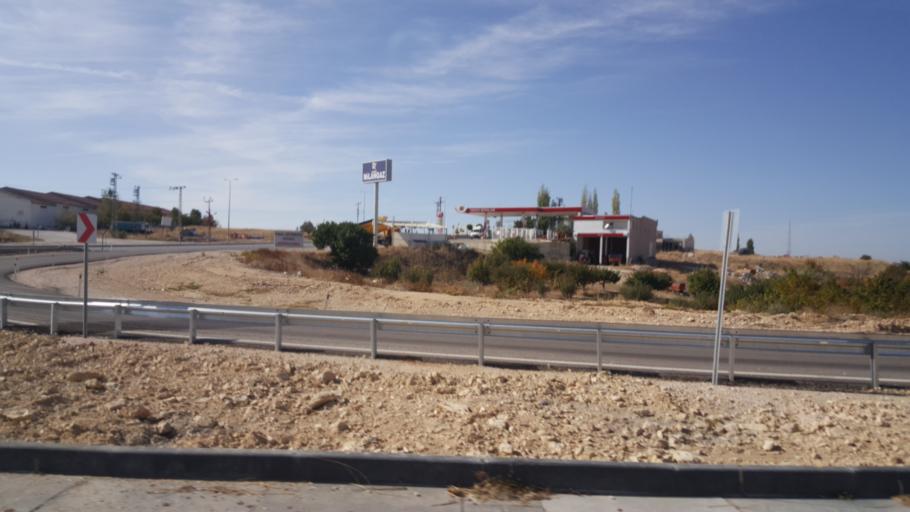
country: TR
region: Ankara
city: Haymana
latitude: 39.4308
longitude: 32.5217
